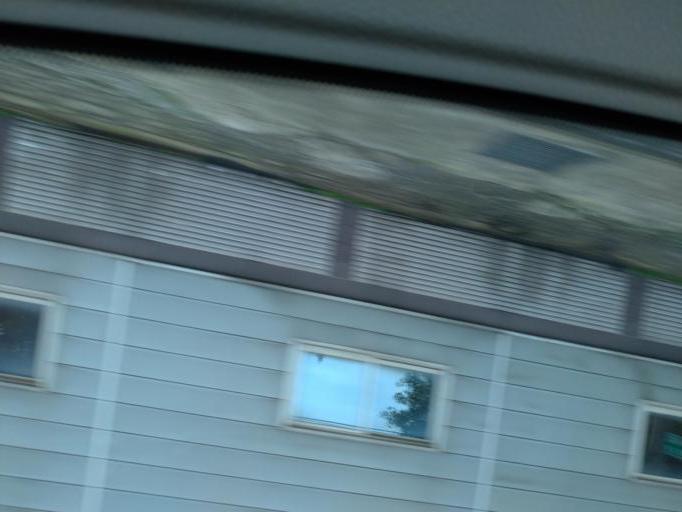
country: TW
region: Taipei
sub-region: Taipei
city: Banqiao
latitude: 24.9317
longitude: 121.4083
